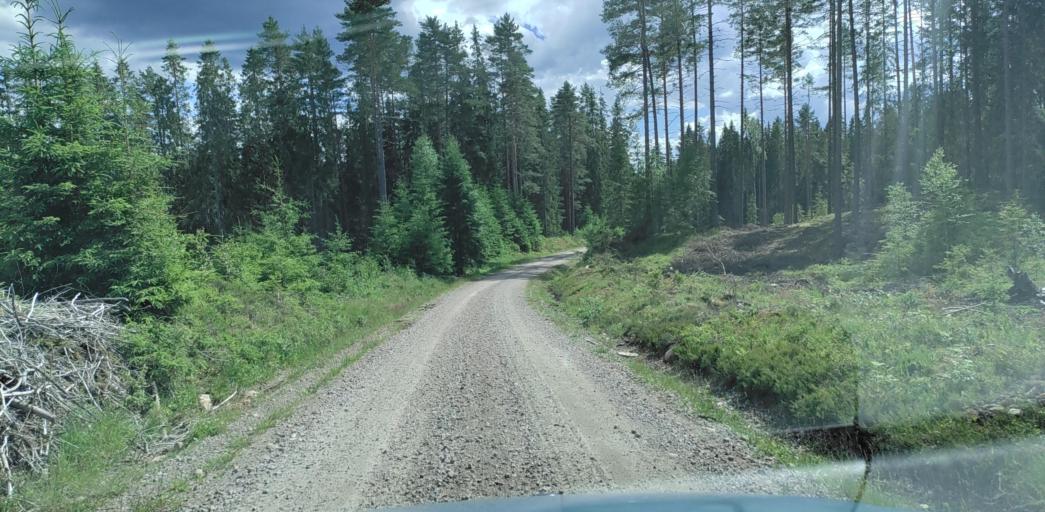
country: SE
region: Vaermland
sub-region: Hagfors Kommun
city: Ekshaerad
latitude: 60.0436
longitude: 13.3117
